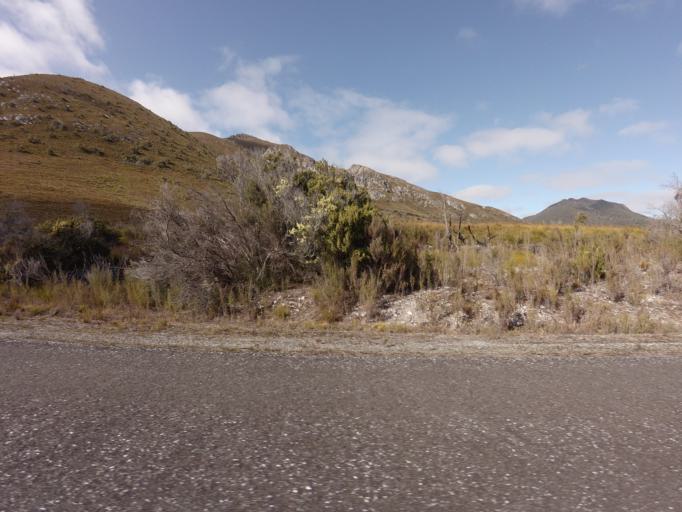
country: AU
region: Tasmania
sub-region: Huon Valley
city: Geeveston
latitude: -42.8622
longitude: 146.2099
